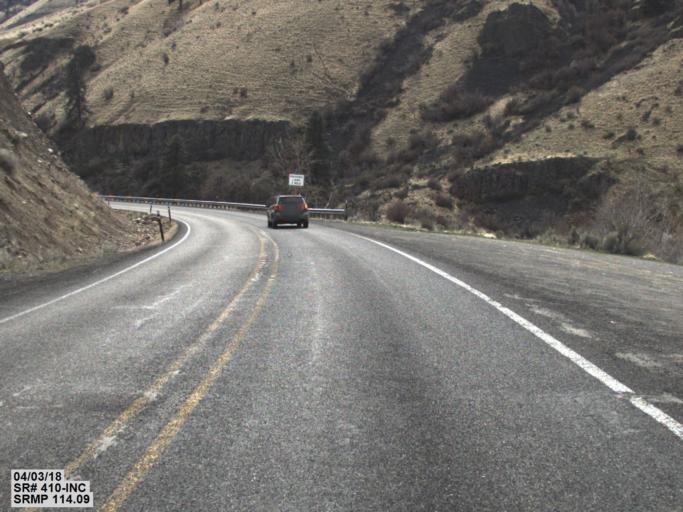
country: US
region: Washington
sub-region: Yakima County
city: Tieton
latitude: 46.7612
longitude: -120.8296
